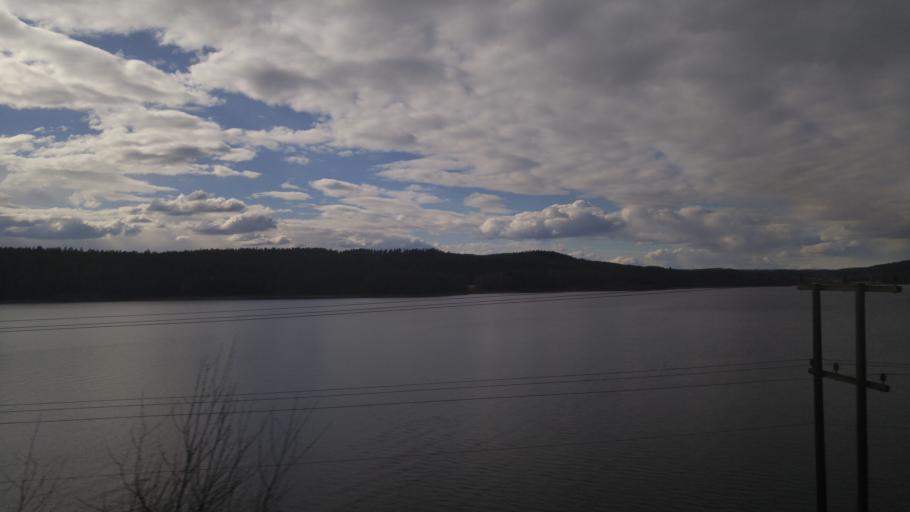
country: NO
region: Hedmark
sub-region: Stange
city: Stange
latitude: 60.5905
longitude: 11.2843
